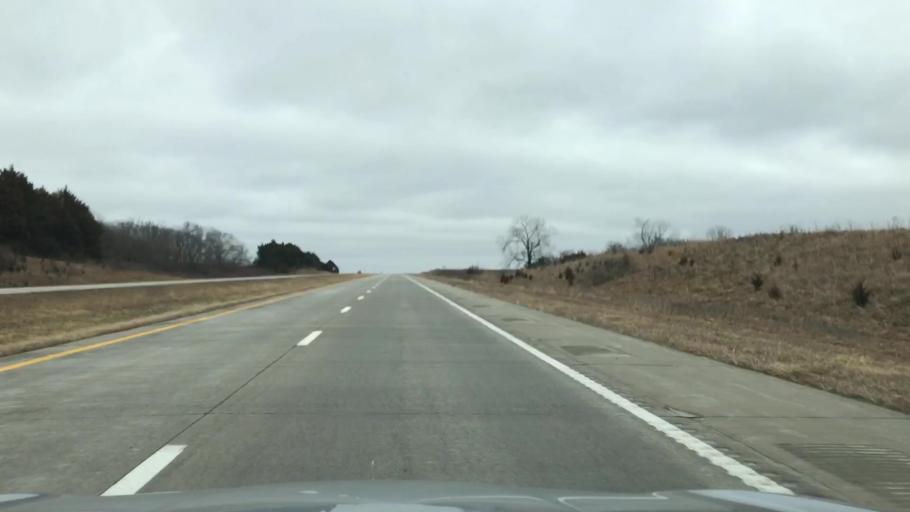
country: US
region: Missouri
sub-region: Caldwell County
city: Hamilton
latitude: 39.7351
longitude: -93.8608
